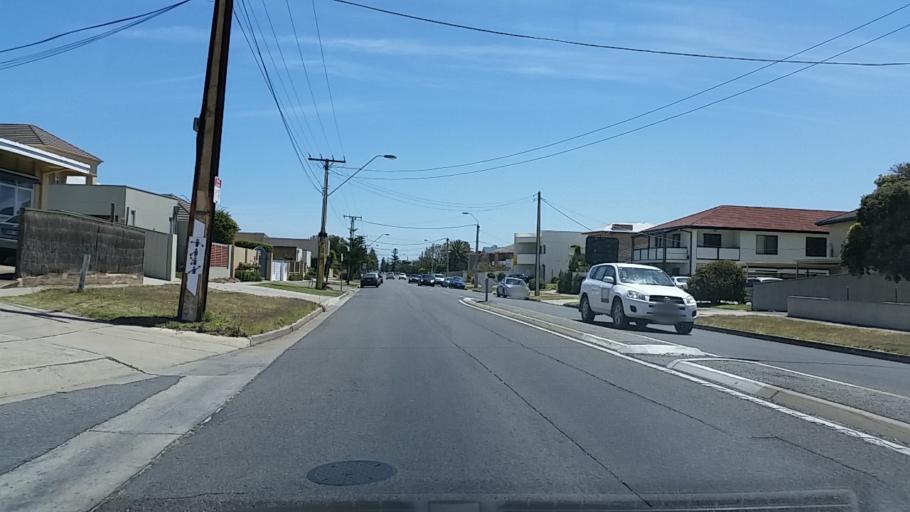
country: AU
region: South Australia
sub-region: Charles Sturt
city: Henley Beach
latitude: -34.9379
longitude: 138.4999
